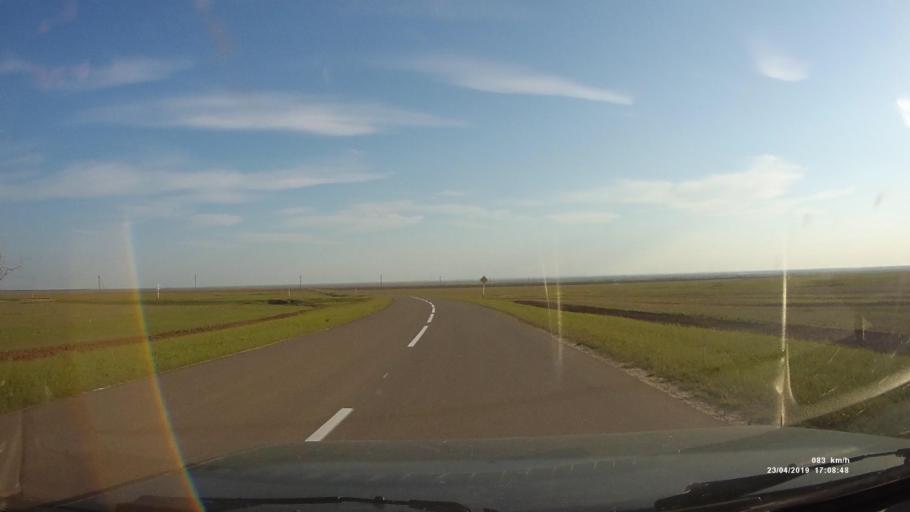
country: RU
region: Kalmykiya
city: Priyutnoye
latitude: 46.2671
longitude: 43.4848
